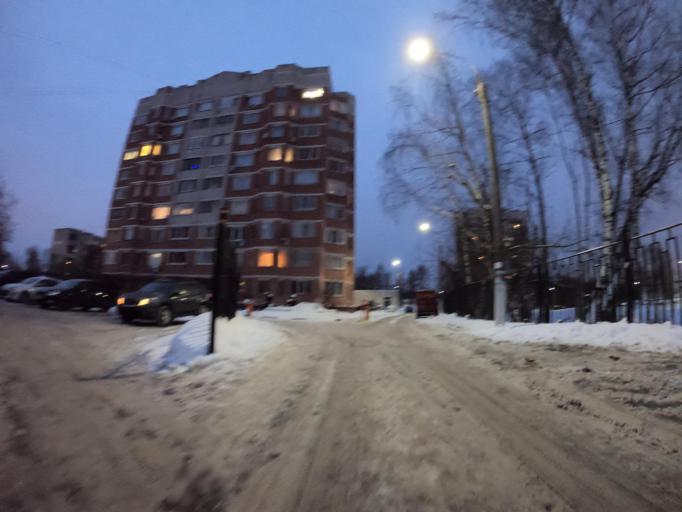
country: RU
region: Moskovskaya
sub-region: Podol'skiy Rayon
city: Podol'sk
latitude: 55.4196
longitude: 37.5221
